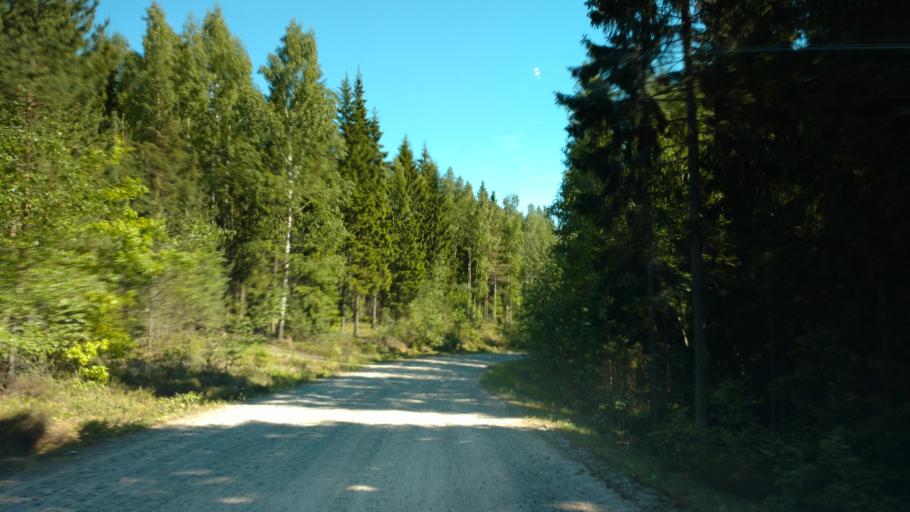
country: FI
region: Varsinais-Suomi
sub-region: Salo
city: Halikko
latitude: 60.4285
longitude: 22.9593
